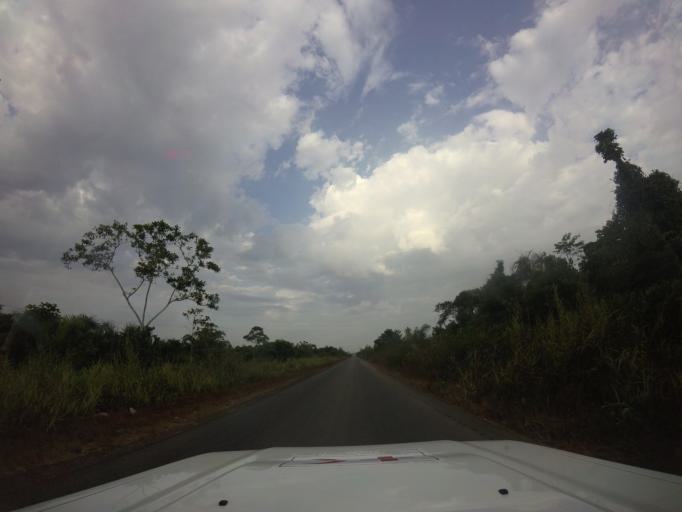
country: LR
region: Bomi
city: Tubmanburg
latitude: 6.7121
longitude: -10.9536
